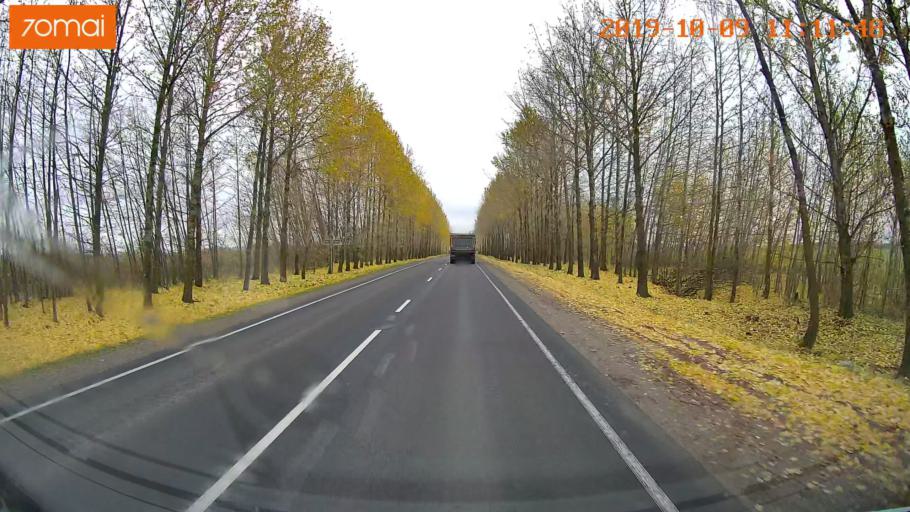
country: RU
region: Vologda
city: Vologda
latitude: 59.1716
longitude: 39.8240
